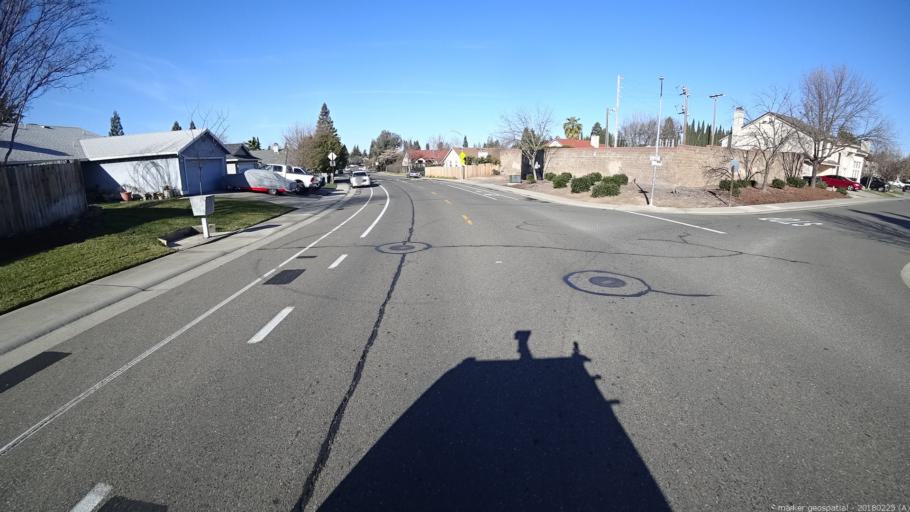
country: US
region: California
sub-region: Sacramento County
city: North Highlands
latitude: 38.7232
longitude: -121.3825
